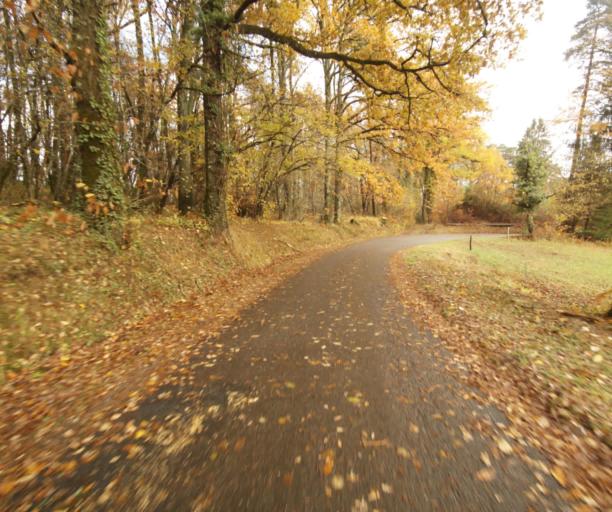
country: FR
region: Limousin
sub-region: Departement de la Correze
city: Saint-Mexant
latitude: 45.2347
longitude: 1.6360
